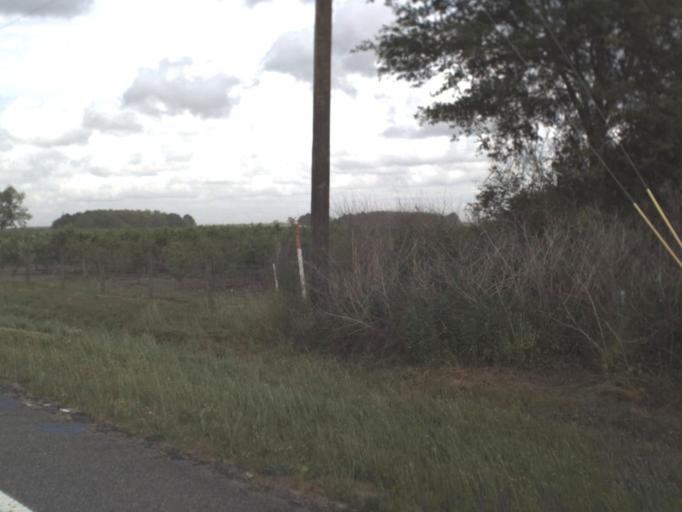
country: US
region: Florida
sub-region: Santa Rosa County
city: Point Baker
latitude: 30.7488
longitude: -87.0934
